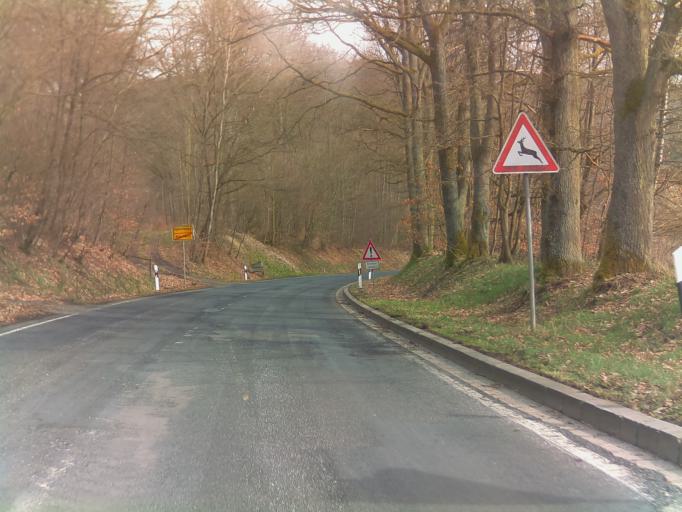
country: DE
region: Rheinland-Pfalz
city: Munchwald
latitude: 49.9002
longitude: 7.6706
